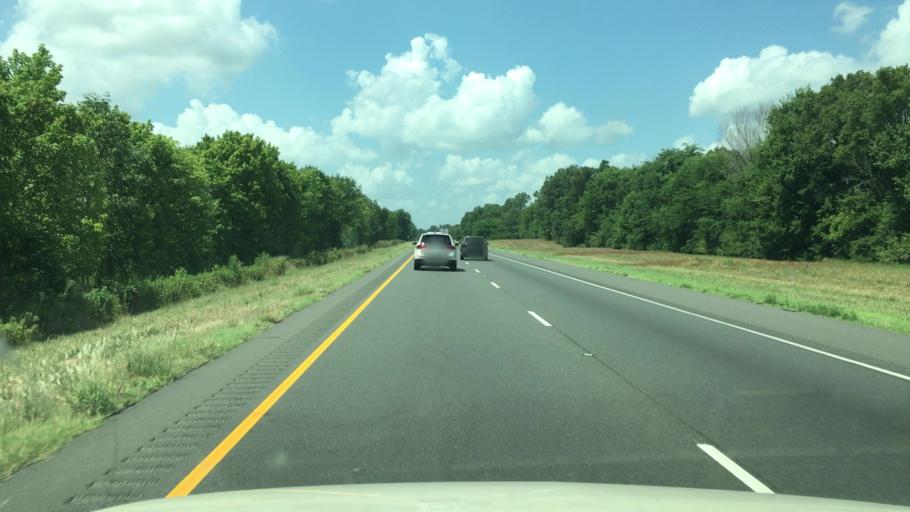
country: US
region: Arkansas
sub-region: Hempstead County
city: Hope
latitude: 33.7232
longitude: -93.5507
